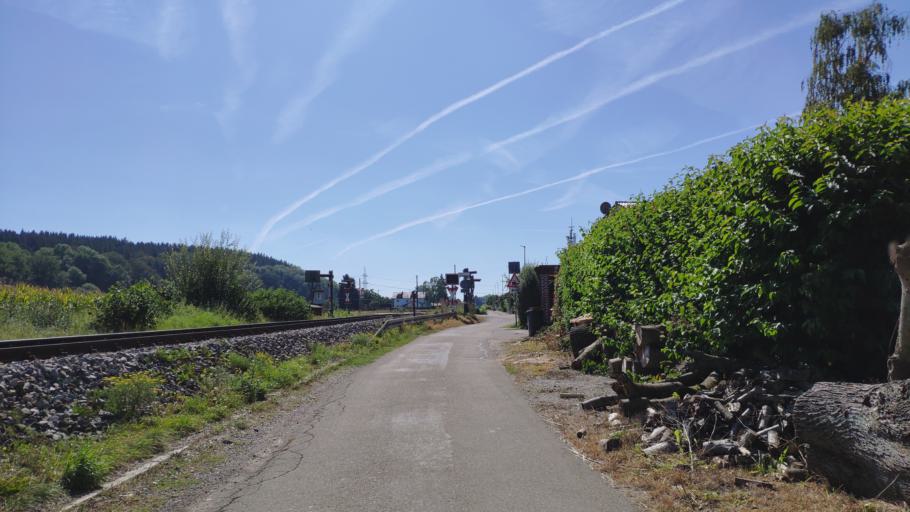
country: DE
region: Bavaria
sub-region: Swabia
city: Senden
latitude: 48.3439
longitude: 10.0393
